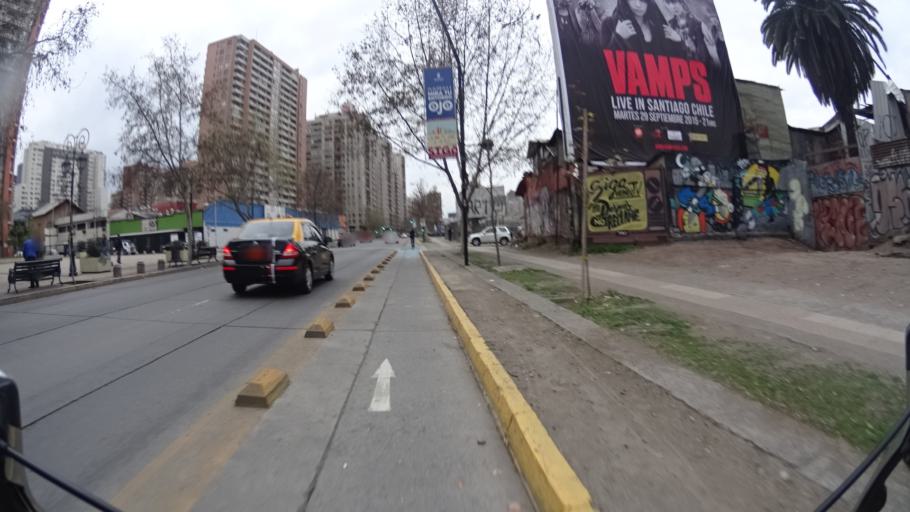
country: CL
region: Santiago Metropolitan
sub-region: Provincia de Santiago
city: Santiago
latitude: -33.4515
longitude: -70.6485
